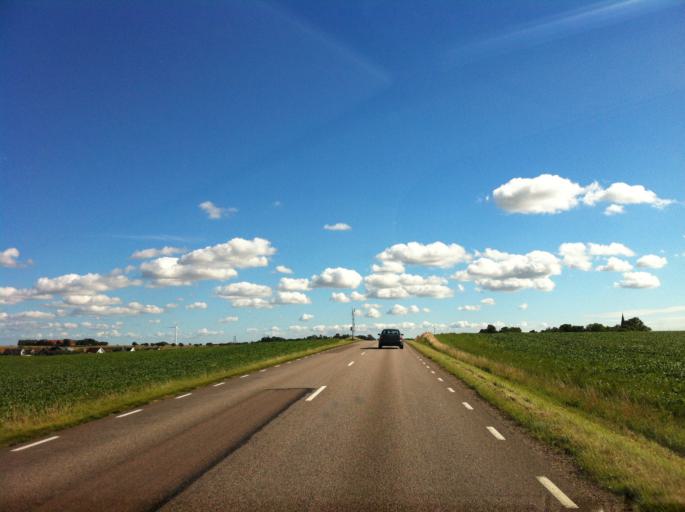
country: SE
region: Skane
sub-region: Svalovs Kommun
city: Kagerod
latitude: 56.0294
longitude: 13.1069
